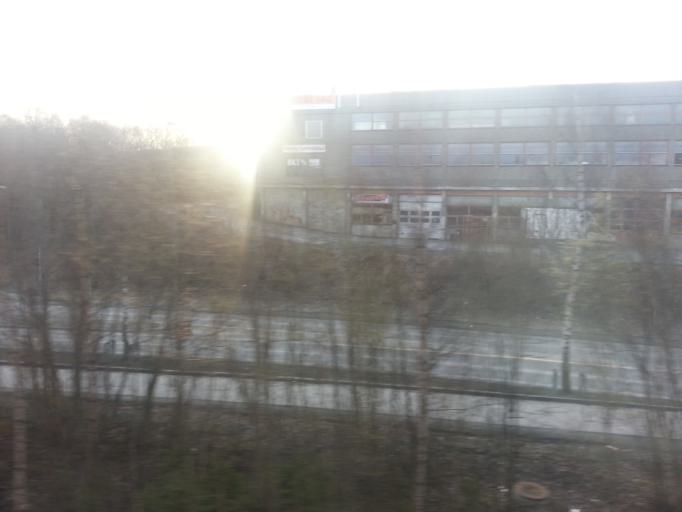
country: NO
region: Sor-Trondelag
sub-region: Trondheim
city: Trondheim
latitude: 63.3545
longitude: 10.3582
